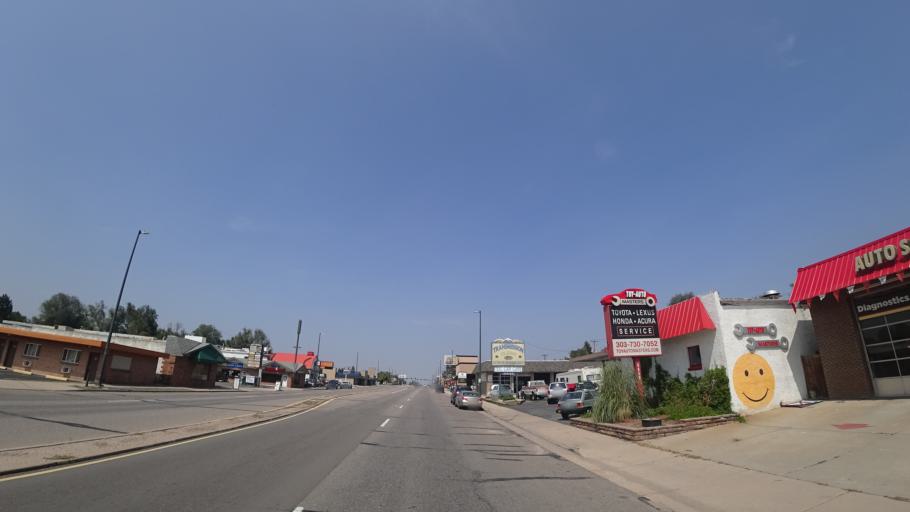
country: US
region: Colorado
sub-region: Arapahoe County
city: Englewood
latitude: 39.6356
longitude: -104.9878
